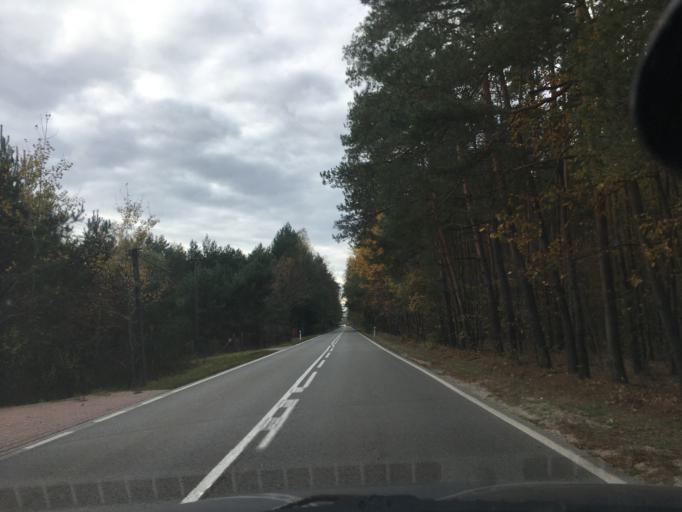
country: PL
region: Masovian Voivodeship
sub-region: Powiat piaseczynski
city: Prazmow
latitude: 51.9842
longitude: 20.9104
